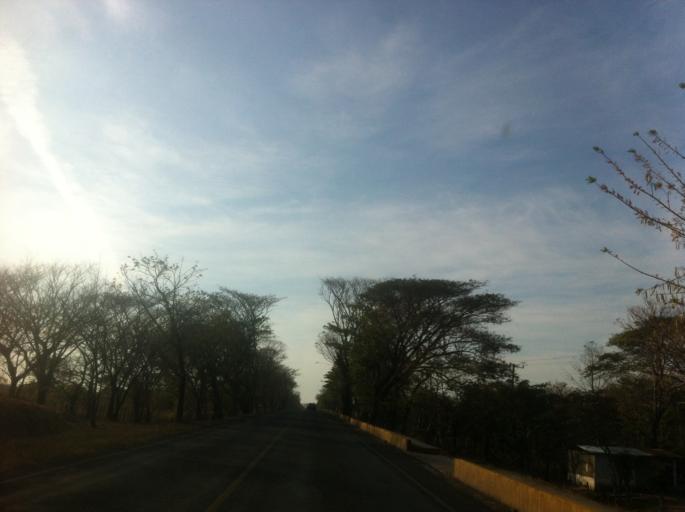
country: NI
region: Rivas
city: Cardenas
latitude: 11.2538
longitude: -85.6331
